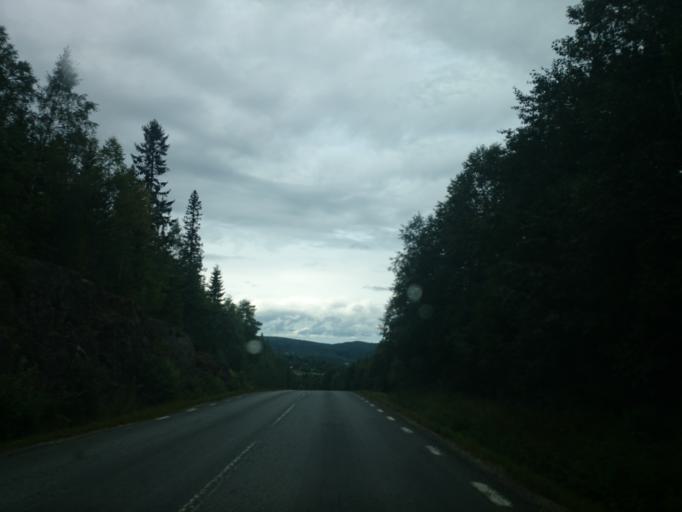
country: SE
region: Vaesternorrland
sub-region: Kramfors Kommun
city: Nordingra
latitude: 62.9791
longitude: 18.2596
